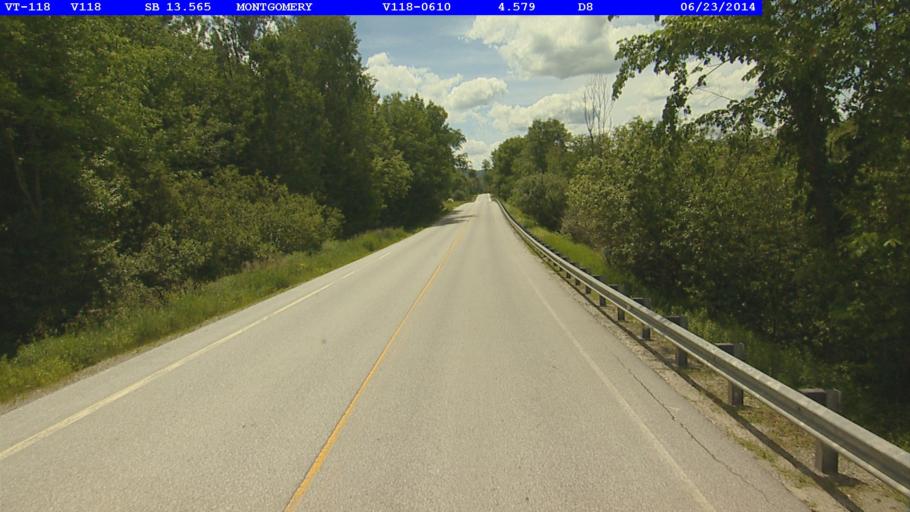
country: US
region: Vermont
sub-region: Franklin County
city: Richford
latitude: 44.8634
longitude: -72.6097
